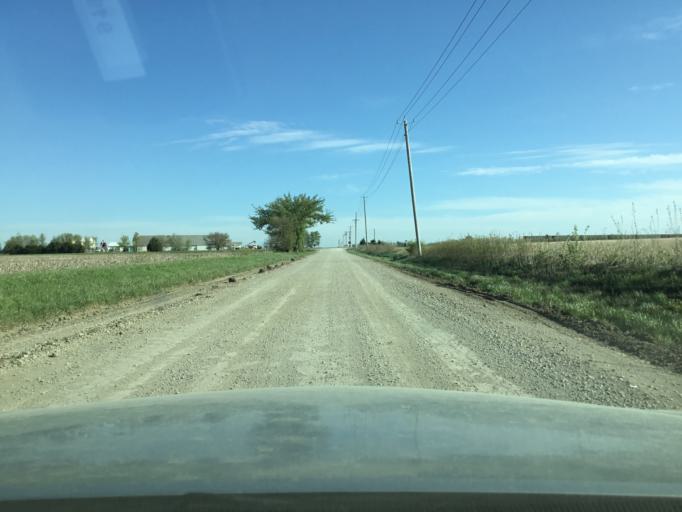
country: US
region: Kansas
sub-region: Neosho County
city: Chanute
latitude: 37.6583
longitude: -95.4892
